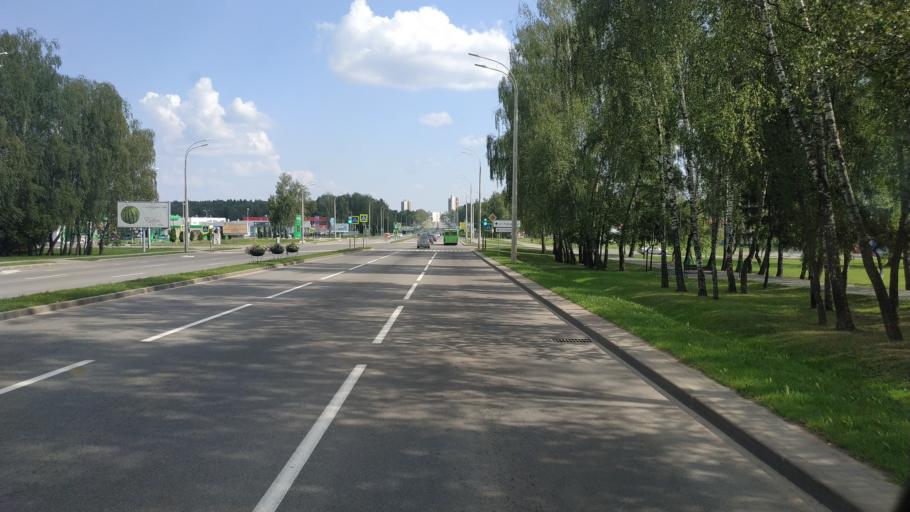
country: BY
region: Mogilev
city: Buynichy
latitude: 53.9291
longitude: 30.2662
